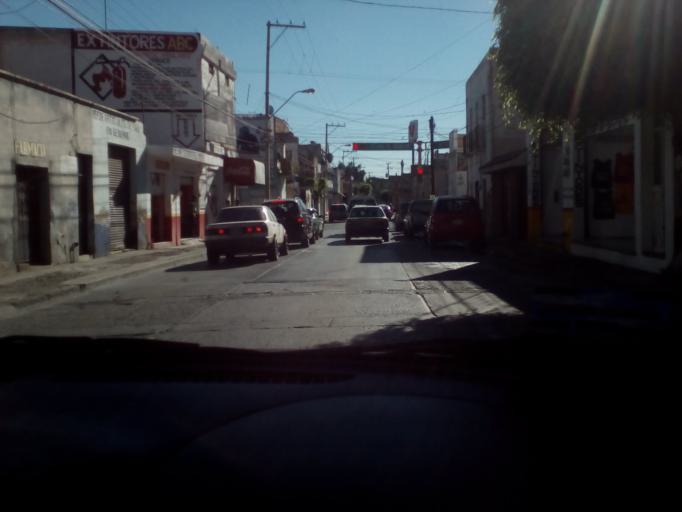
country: MX
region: Guanajuato
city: Leon
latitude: 21.1302
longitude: -101.6890
